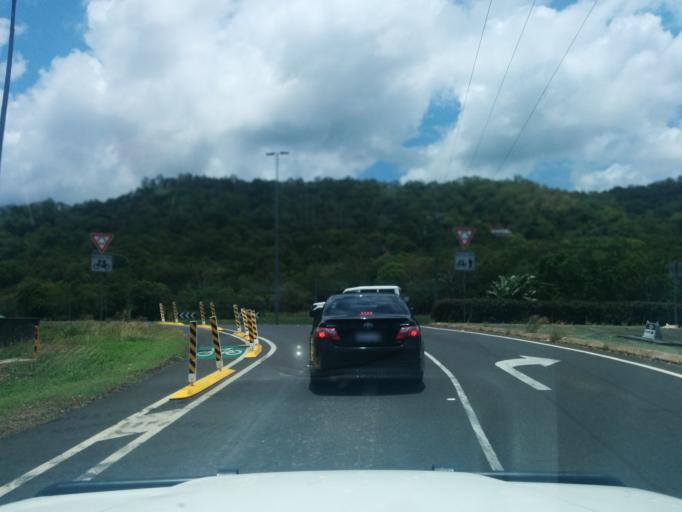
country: AU
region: Queensland
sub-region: Cairns
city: Trinity Beach
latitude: -16.8112
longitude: 145.6938
